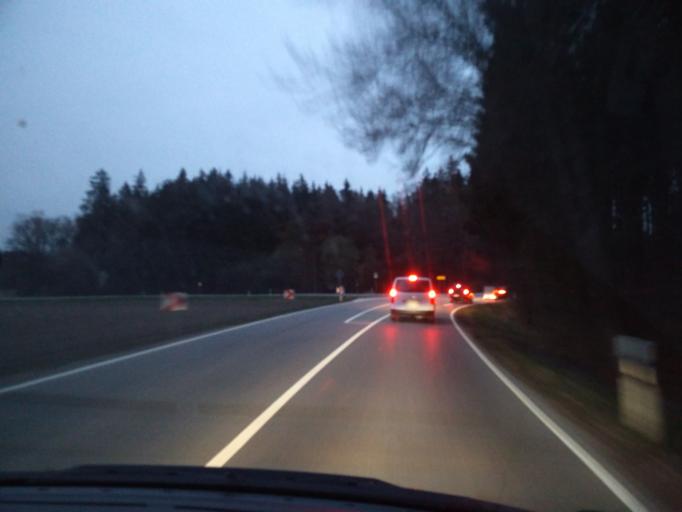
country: DE
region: Bavaria
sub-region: Upper Bavaria
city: Rechtmehring
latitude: 48.0872
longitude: 12.1567
